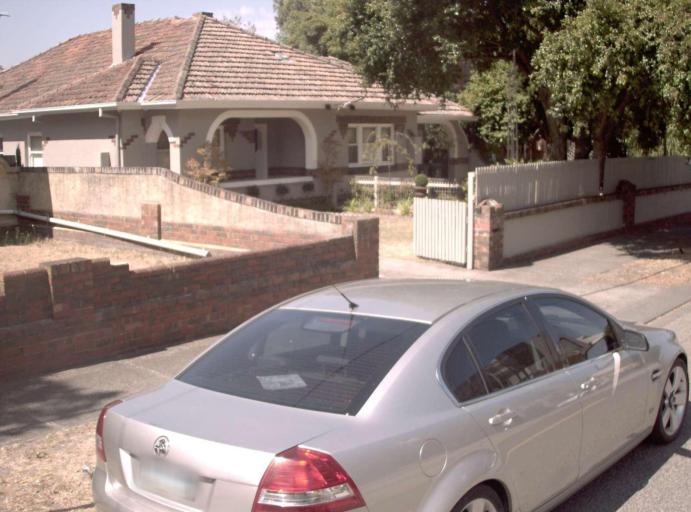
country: AU
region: Victoria
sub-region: Stonnington
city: Malvern East
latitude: -37.8757
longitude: 145.0461
